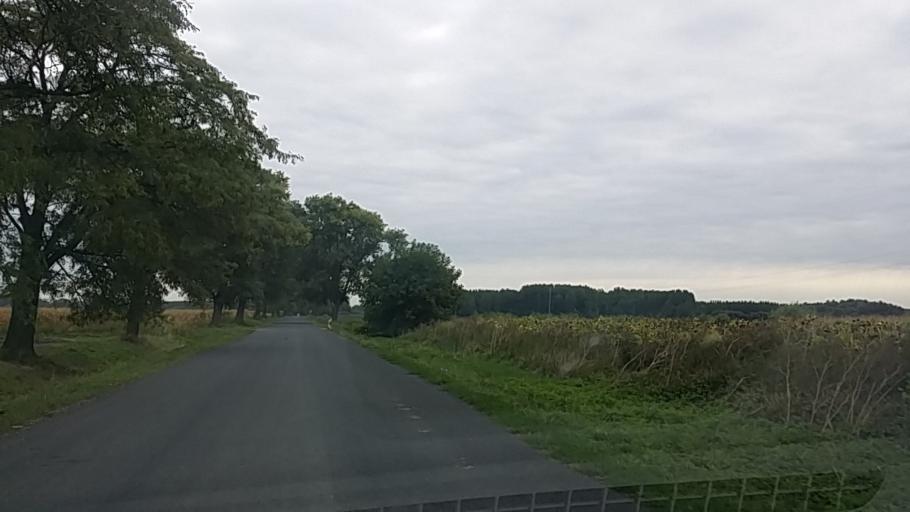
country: HU
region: Gyor-Moson-Sopron
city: Kapuvar
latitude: 47.6436
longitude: 17.0897
